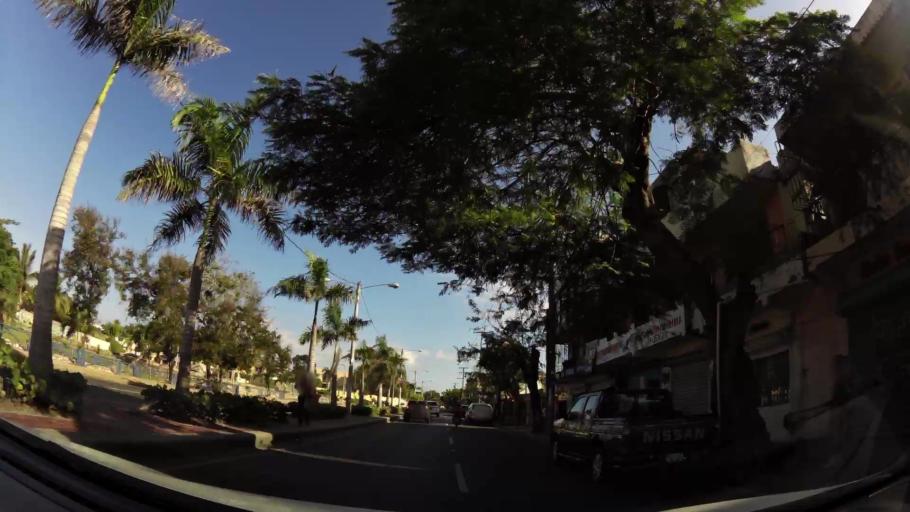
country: DO
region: Nacional
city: San Carlos
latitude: 18.4784
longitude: -69.8778
